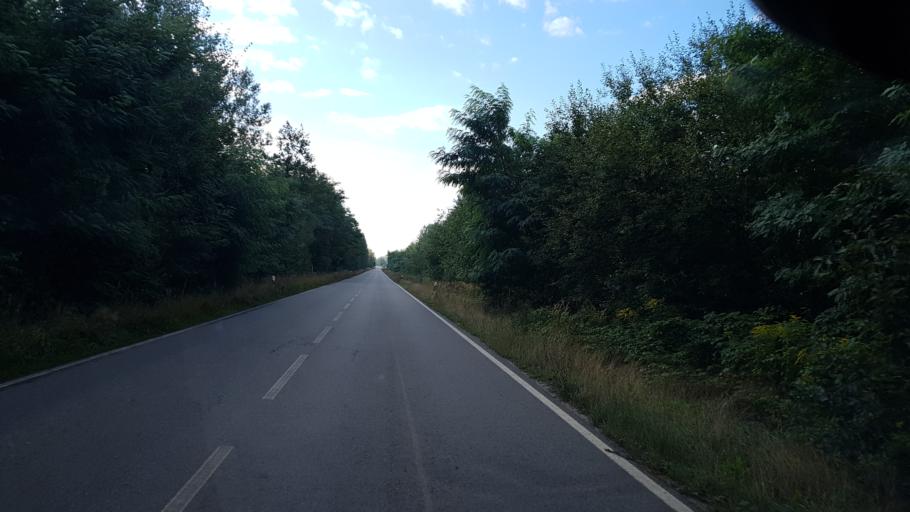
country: DE
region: Brandenburg
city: Welzow
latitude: 51.5499
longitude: 14.2275
